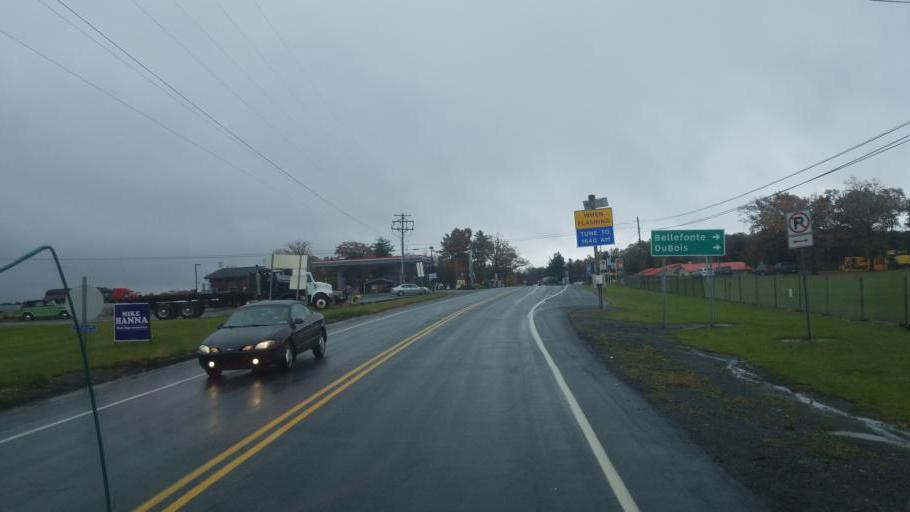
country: US
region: Pennsylvania
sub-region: Centre County
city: Milesburg
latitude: 41.0269
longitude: -77.9369
